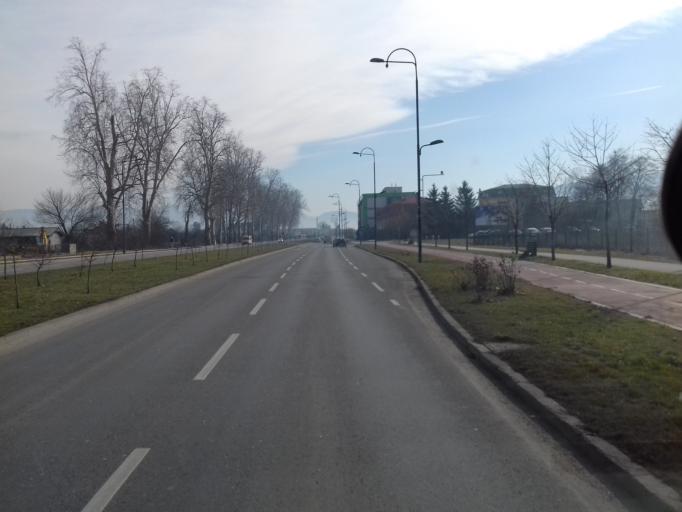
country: BA
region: Federation of Bosnia and Herzegovina
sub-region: Kanton Sarajevo
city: Sarajevo
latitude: 43.8279
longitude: 18.3151
